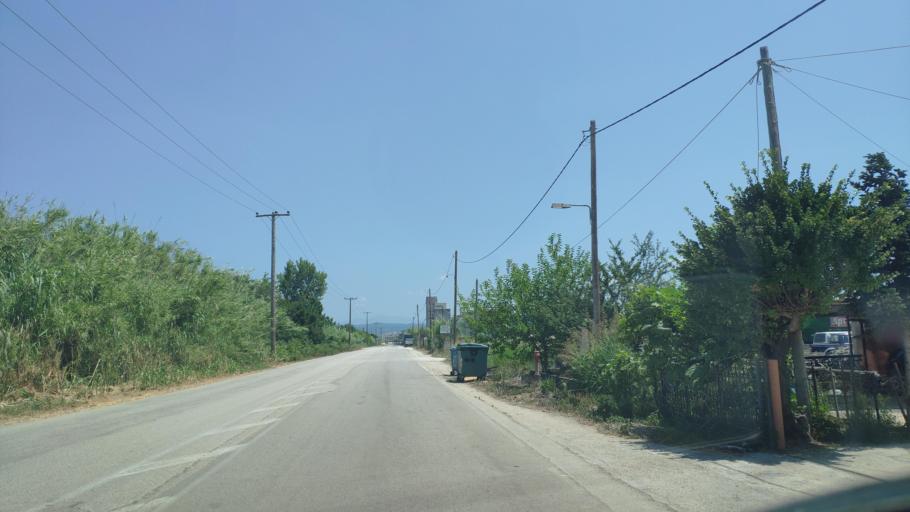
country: GR
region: Epirus
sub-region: Nomos Artas
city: Kostakioi
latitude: 39.1255
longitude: 20.9425
